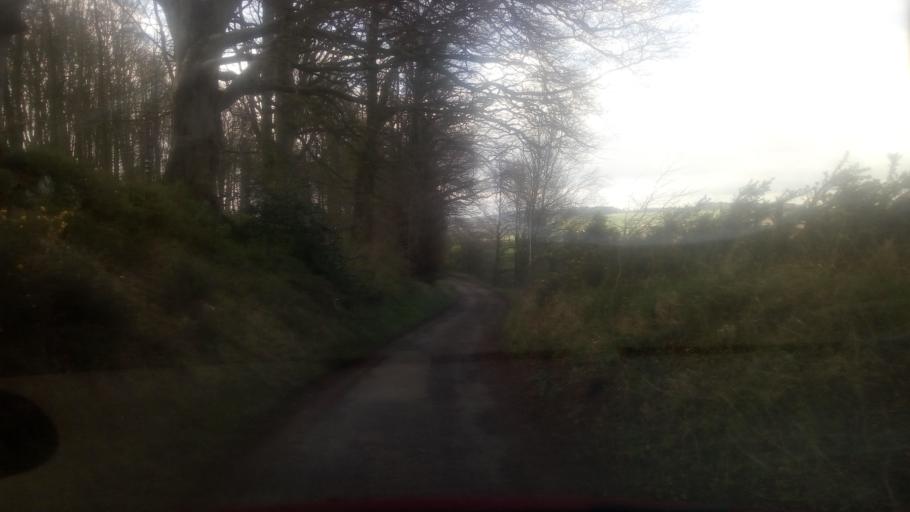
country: GB
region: Scotland
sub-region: The Scottish Borders
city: Jedburgh
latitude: 55.4976
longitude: -2.5338
